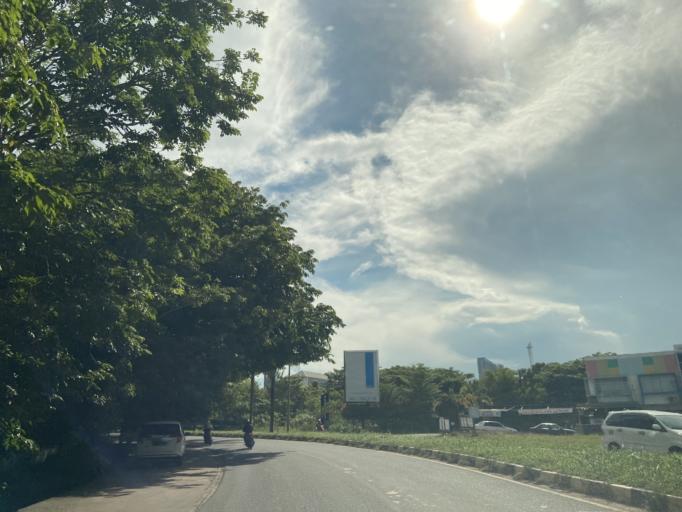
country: SG
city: Singapore
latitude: 1.1159
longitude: 104.0561
